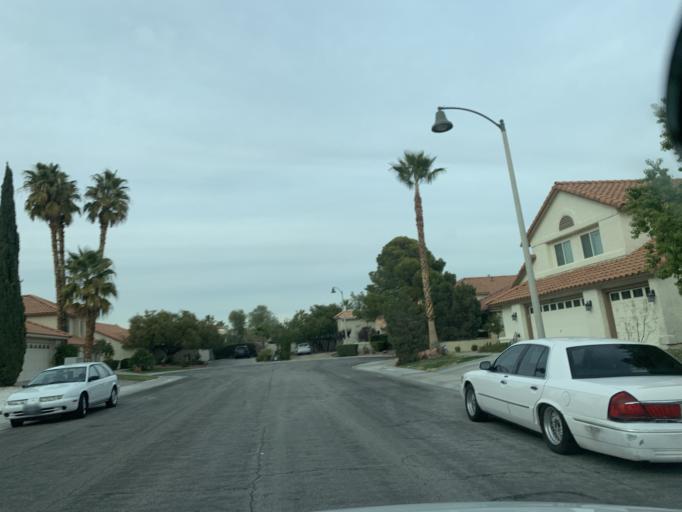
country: US
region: Nevada
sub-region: Clark County
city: Summerlin South
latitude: 36.1420
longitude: -115.2942
